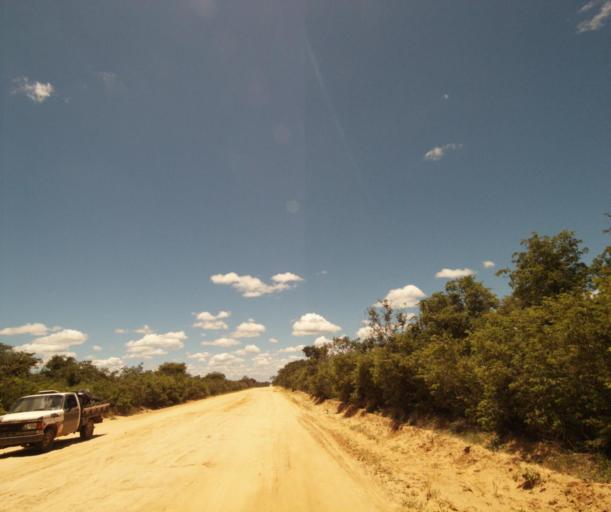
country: BR
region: Bahia
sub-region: Carinhanha
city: Carinhanha
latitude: -14.2398
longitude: -43.8517
